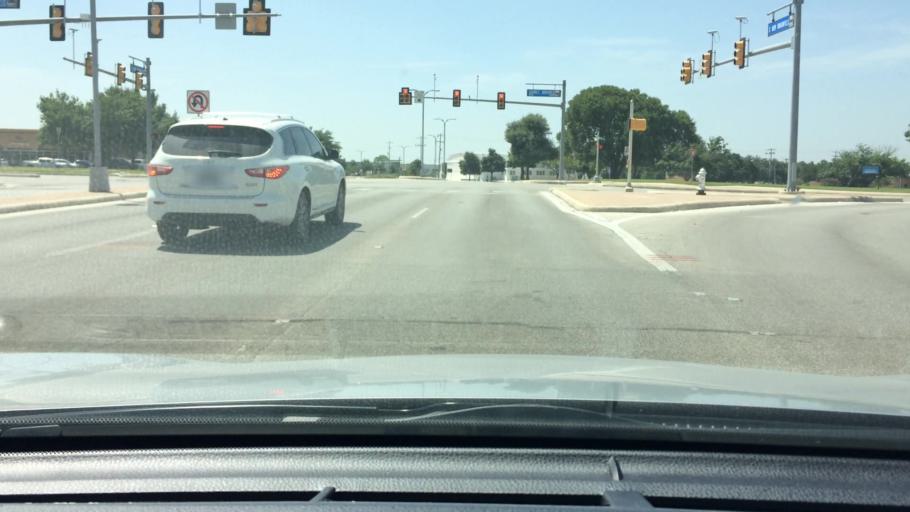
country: US
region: Texas
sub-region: Bexar County
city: San Antonio
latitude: 29.3463
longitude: -98.4453
